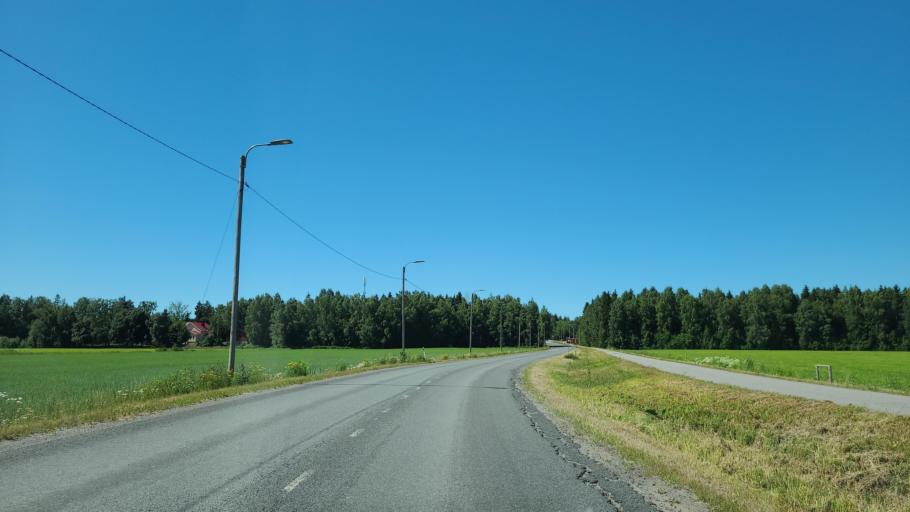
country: FI
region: Ostrobothnia
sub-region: Vaasa
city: Ristinummi
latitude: 63.0554
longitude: 21.7277
